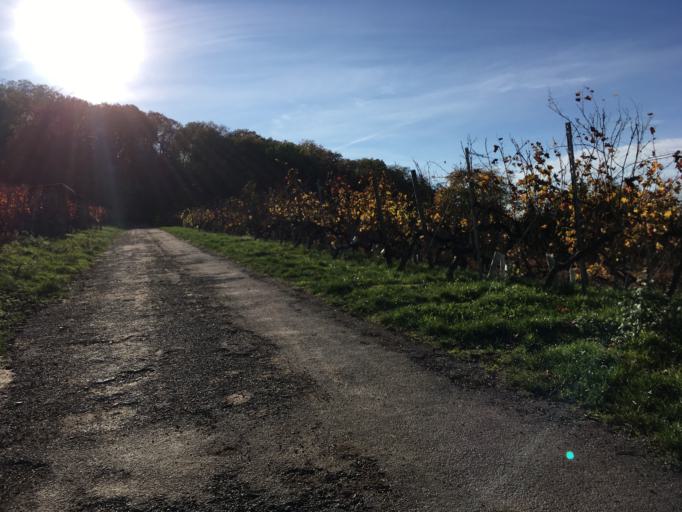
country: DE
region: Baden-Wuerttemberg
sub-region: Karlsruhe Region
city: Oberderdingen
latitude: 49.0494
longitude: 8.8042
